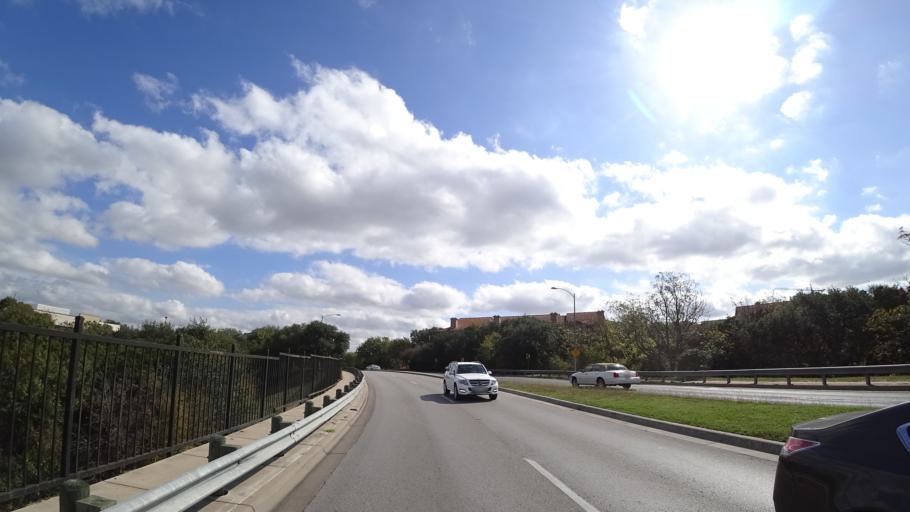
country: US
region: Texas
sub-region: Travis County
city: Wells Branch
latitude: 30.4106
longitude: -97.7196
